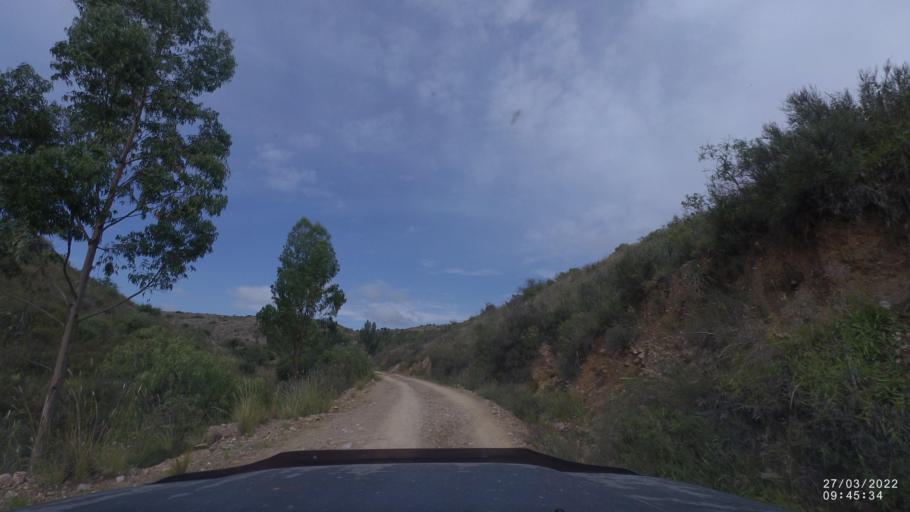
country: BO
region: Cochabamba
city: Cliza
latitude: -17.7511
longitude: -65.9138
